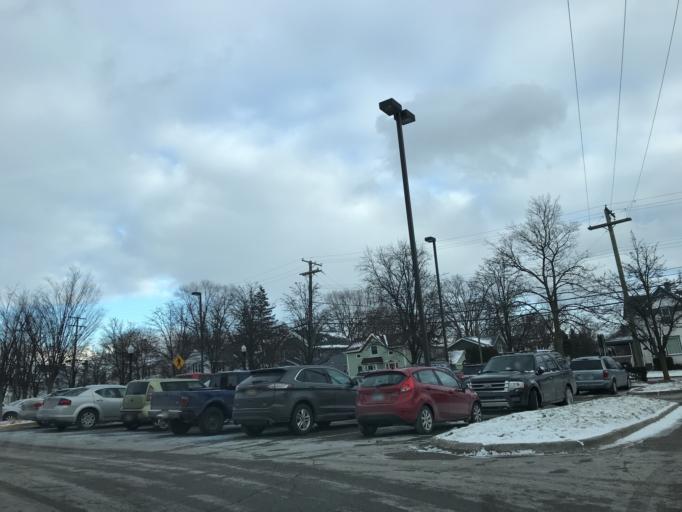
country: US
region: Michigan
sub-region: Wayne County
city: Plymouth
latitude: 42.3712
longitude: -83.4673
